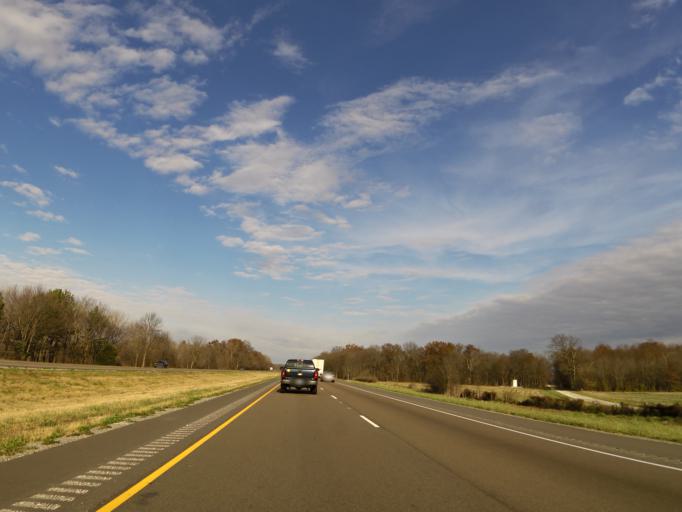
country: US
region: Illinois
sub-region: Washington County
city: Okawville
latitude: 38.4646
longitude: -89.5701
